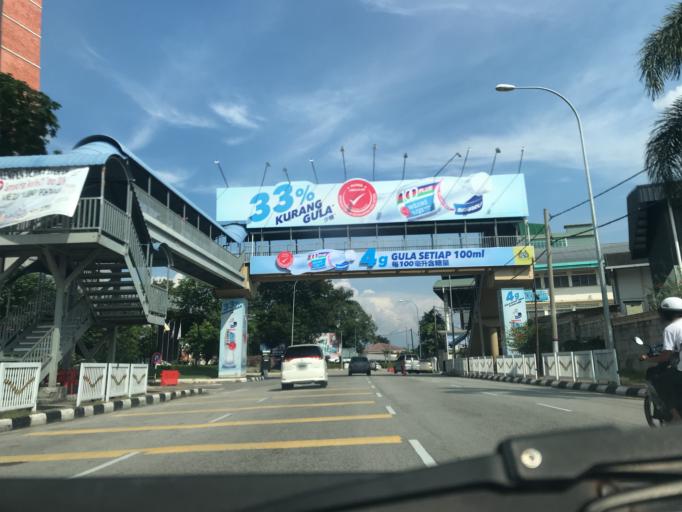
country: MY
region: Perak
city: Ipoh
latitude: 4.5951
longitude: 101.0895
